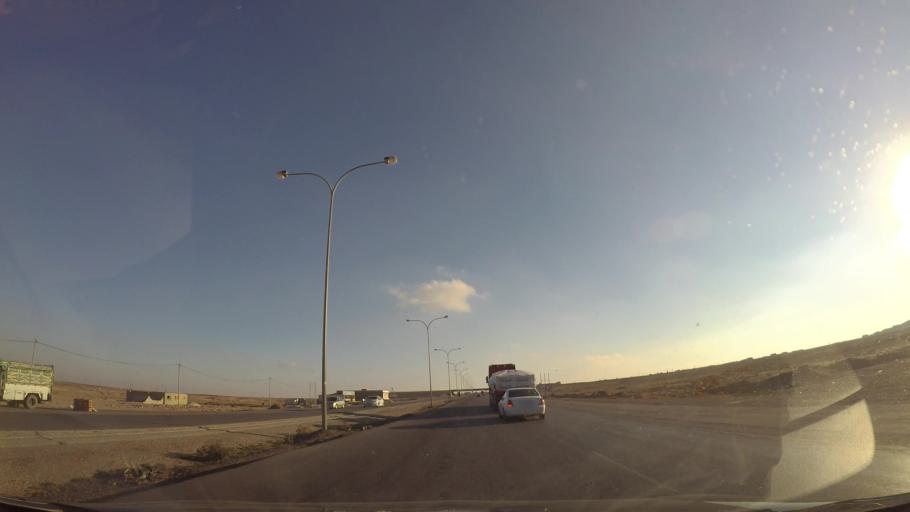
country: JO
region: Tafielah
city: Busayra
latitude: 30.5821
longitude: 35.8006
